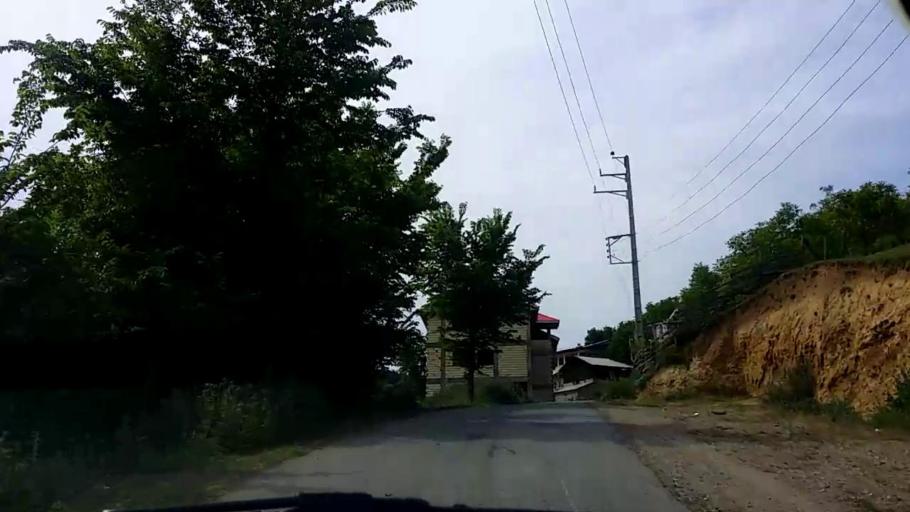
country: IR
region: Mazandaran
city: `Abbasabad
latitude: 36.5522
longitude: 51.1822
